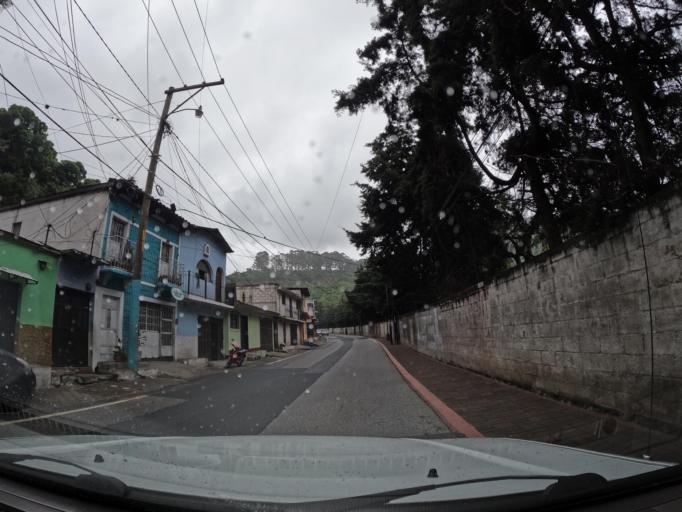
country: GT
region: Sacatepequez
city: Pastores
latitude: 14.5997
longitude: -90.7602
